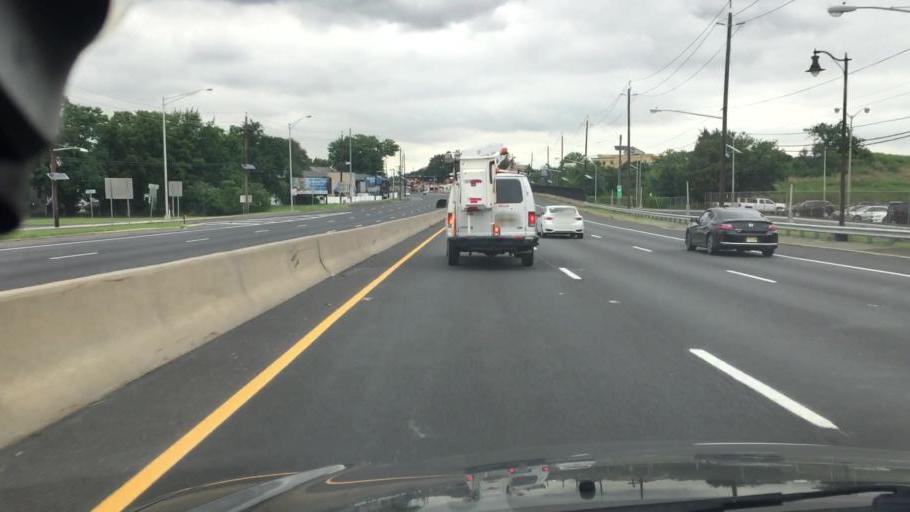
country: US
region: New Jersey
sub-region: Union County
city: Rahway
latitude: 40.6012
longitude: -74.2683
